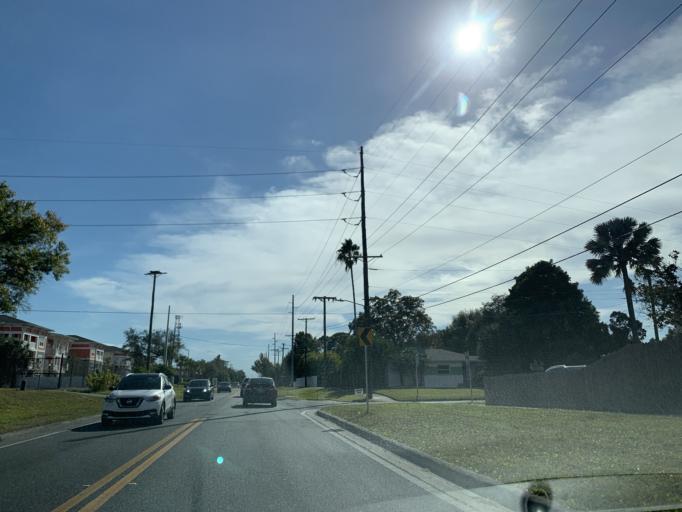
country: US
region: Florida
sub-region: Hillsborough County
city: Tampa
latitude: 27.8909
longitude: -82.5184
